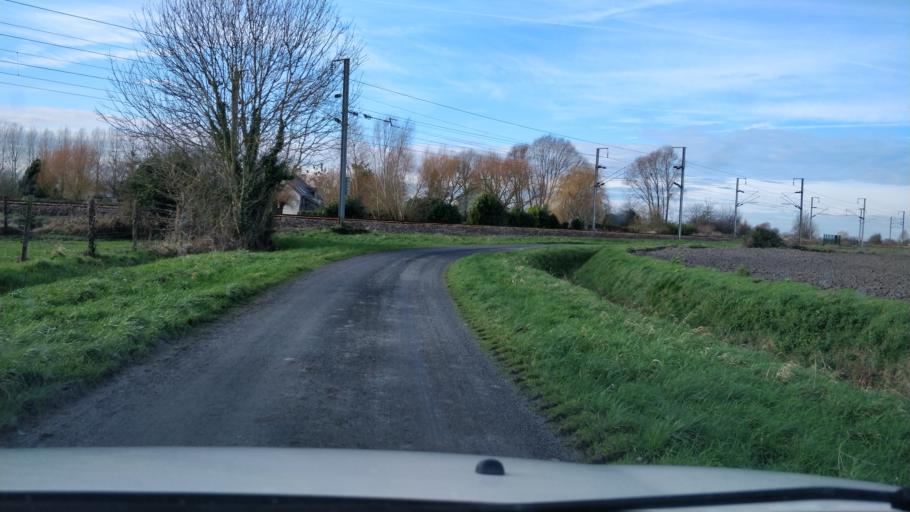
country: FR
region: Brittany
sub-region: Departement d'Ille-et-Vilaine
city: Hirel
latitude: 48.5799
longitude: -1.8102
